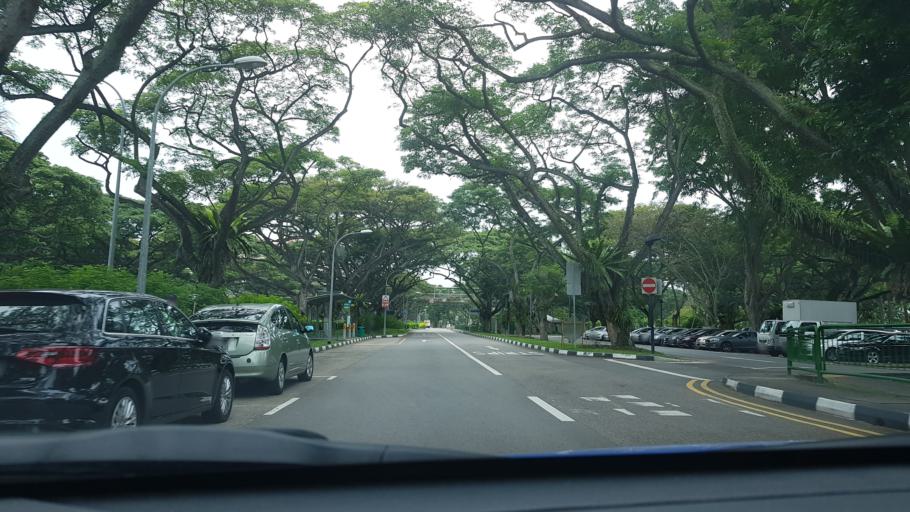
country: SG
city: Singapore
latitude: 1.3031
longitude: 103.9173
